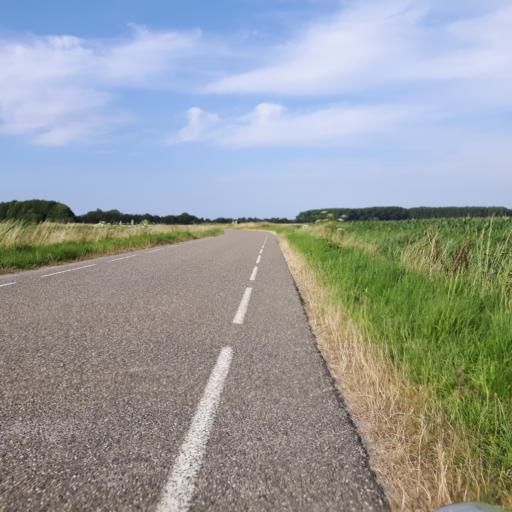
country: NL
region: Zeeland
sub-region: Gemeente Goes
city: Goes
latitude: 51.4750
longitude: 3.9121
